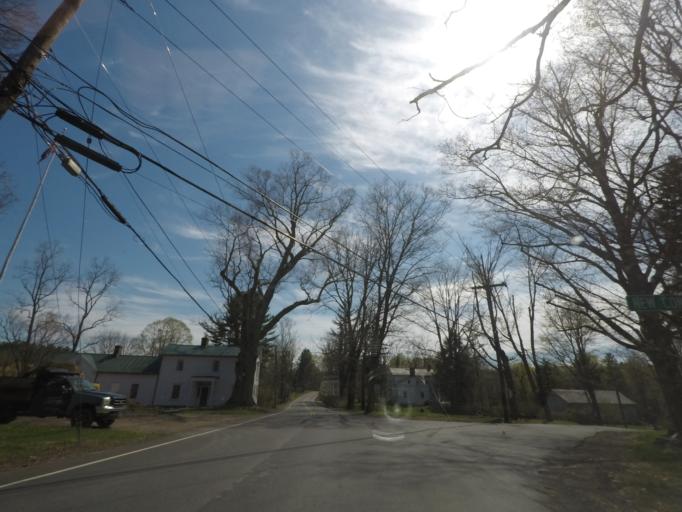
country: US
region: New York
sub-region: Columbia County
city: Chatham
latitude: 42.3953
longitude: -73.5266
